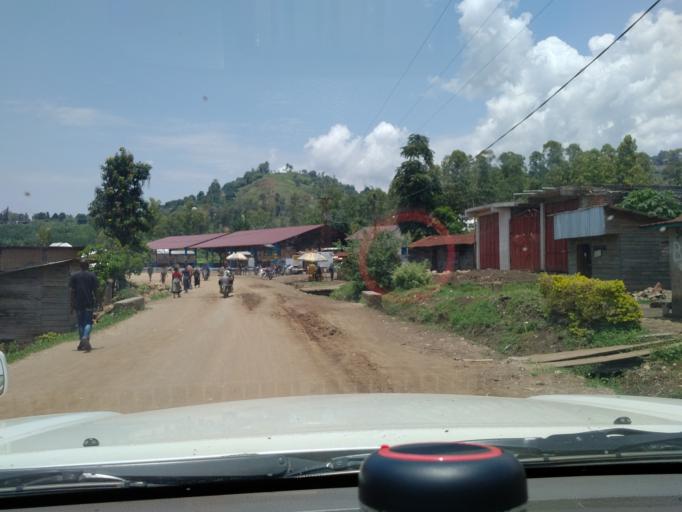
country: CD
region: Nord Kivu
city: Sake
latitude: -1.6983
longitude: 29.0134
